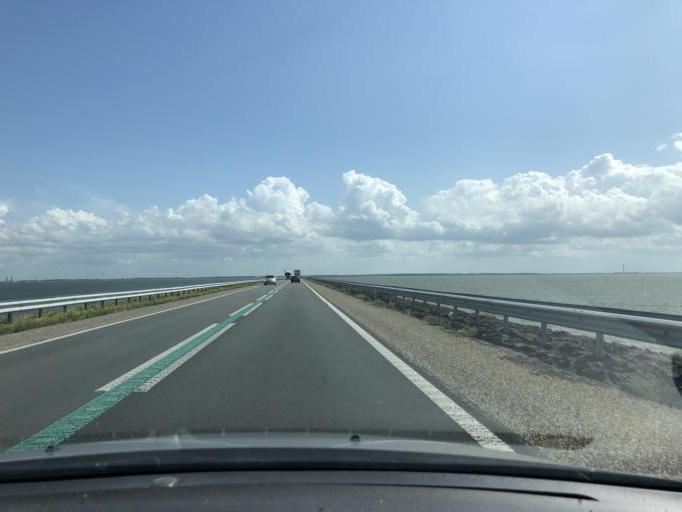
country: NL
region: Flevoland
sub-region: Gemeente Lelystad
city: Lelystad
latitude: 52.6129
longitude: 5.4362
